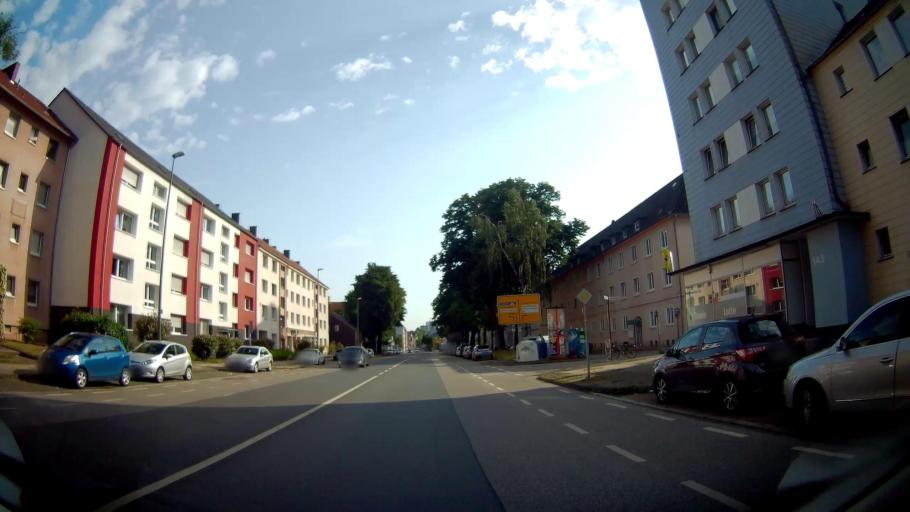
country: DE
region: North Rhine-Westphalia
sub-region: Regierungsbezirk Arnsberg
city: Herne
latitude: 51.5269
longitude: 7.2178
